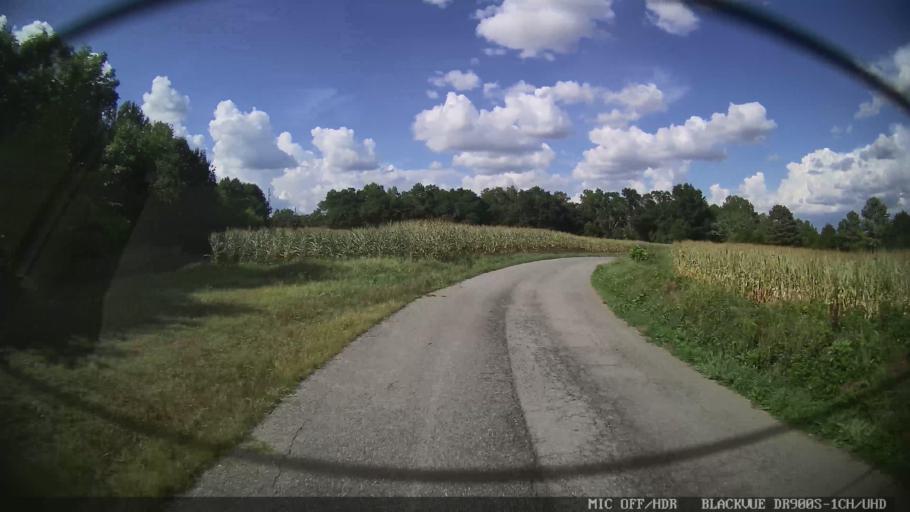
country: US
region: Georgia
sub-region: Bartow County
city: Euharlee
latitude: 34.1005
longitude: -84.9498
